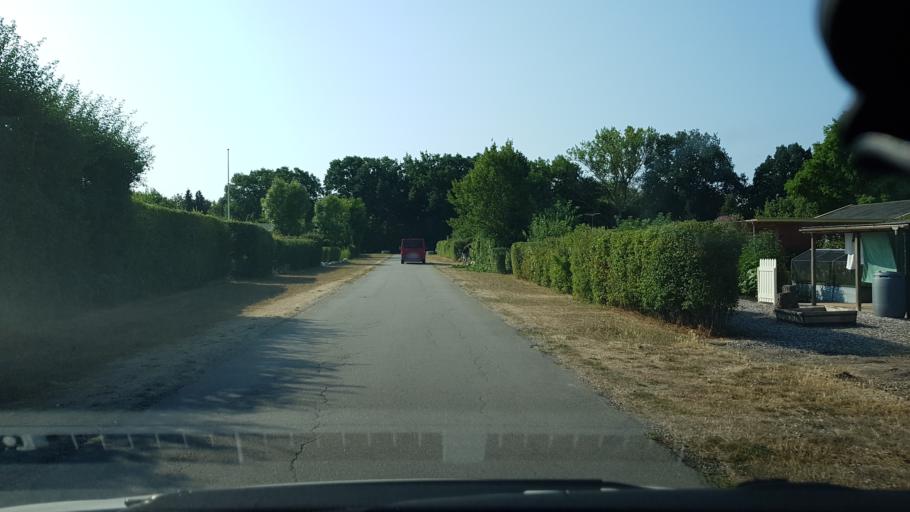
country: DK
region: Capital Region
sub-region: Brondby Kommune
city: Brondbyvester
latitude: 55.6334
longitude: 12.3951
